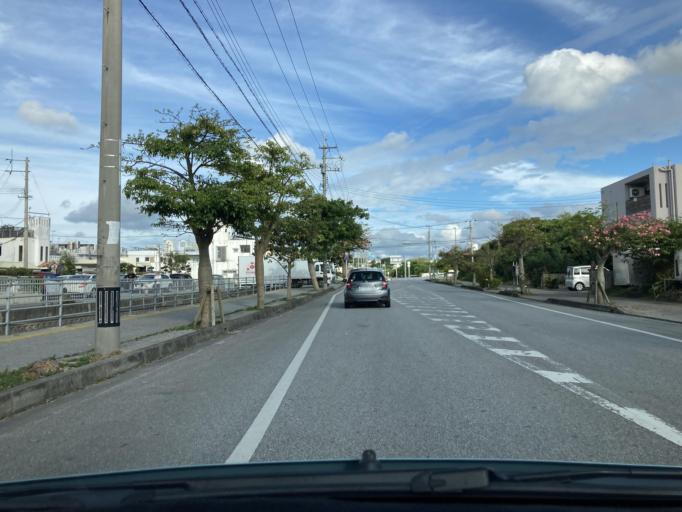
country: JP
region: Okinawa
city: Itoman
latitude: 26.1244
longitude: 127.6766
